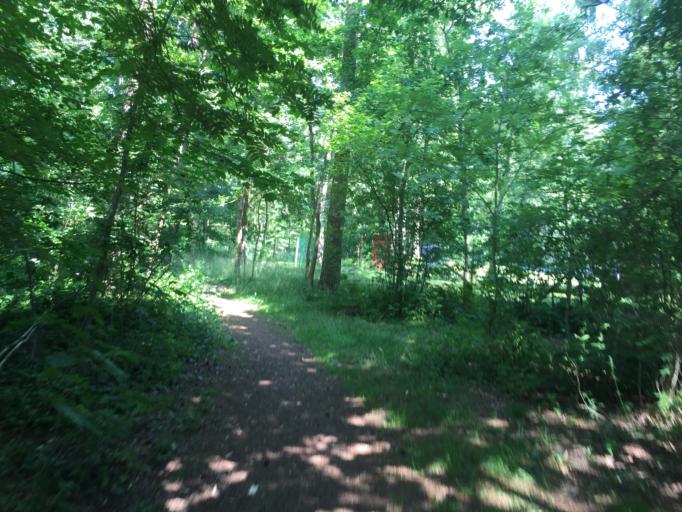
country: SE
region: Skane
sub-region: Lunds Kommun
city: Veberod
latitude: 55.6194
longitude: 13.5088
